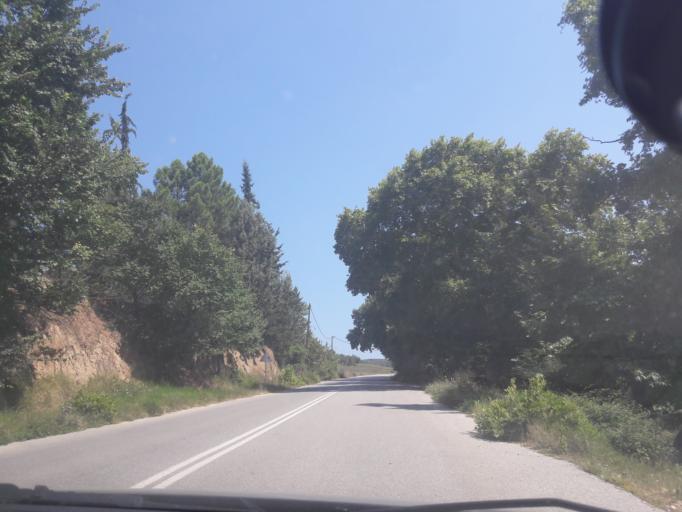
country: GR
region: Central Macedonia
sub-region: Nomos Chalkidikis
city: Megali Panagia
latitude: 40.3698
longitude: 23.6538
